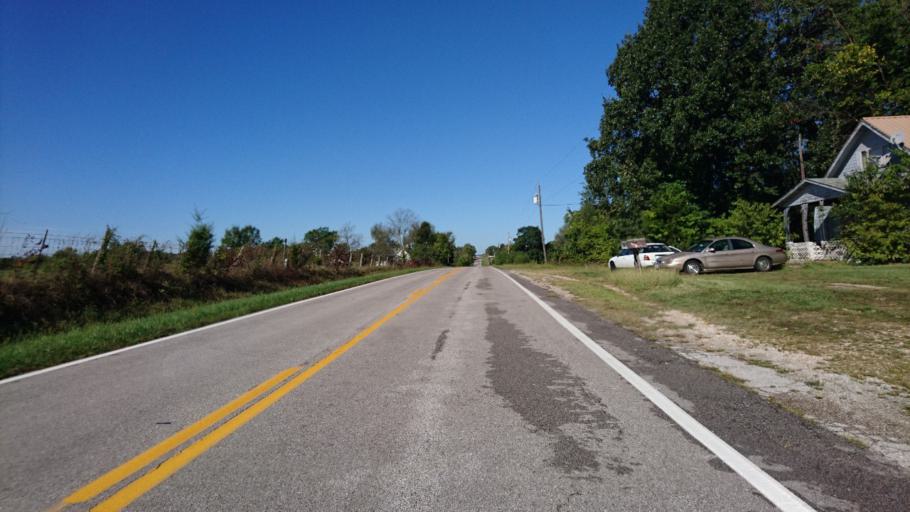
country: US
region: Missouri
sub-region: Greene County
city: Ash Grove
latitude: 37.1937
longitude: -93.6455
